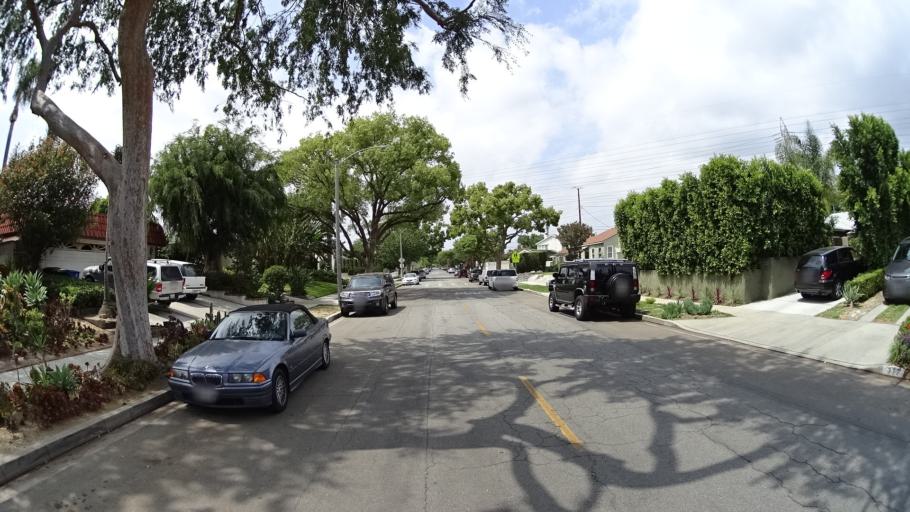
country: US
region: California
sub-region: Los Angeles County
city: Universal City
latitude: 34.1580
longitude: -118.3375
